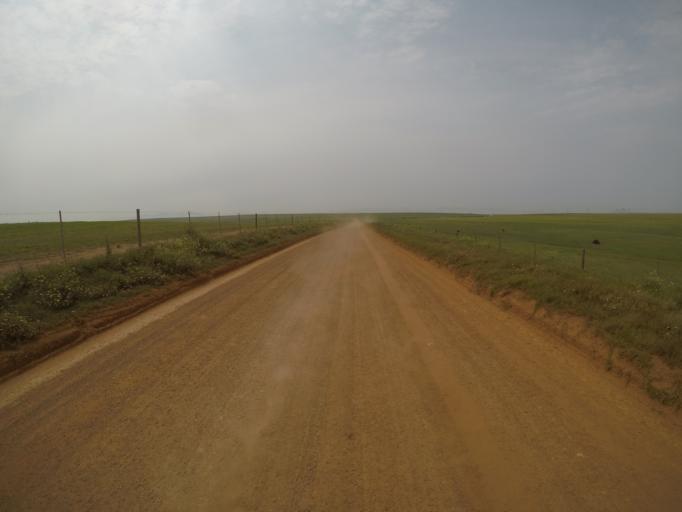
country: ZA
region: Western Cape
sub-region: City of Cape Town
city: Kraaifontein
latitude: -33.7243
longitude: 18.6653
